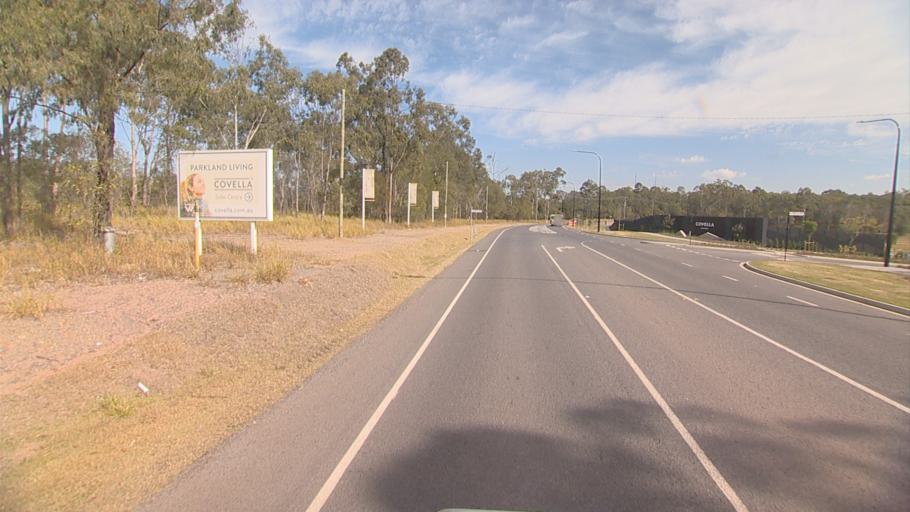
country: AU
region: Queensland
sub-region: Logan
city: North Maclean
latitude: -27.7366
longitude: 152.9751
